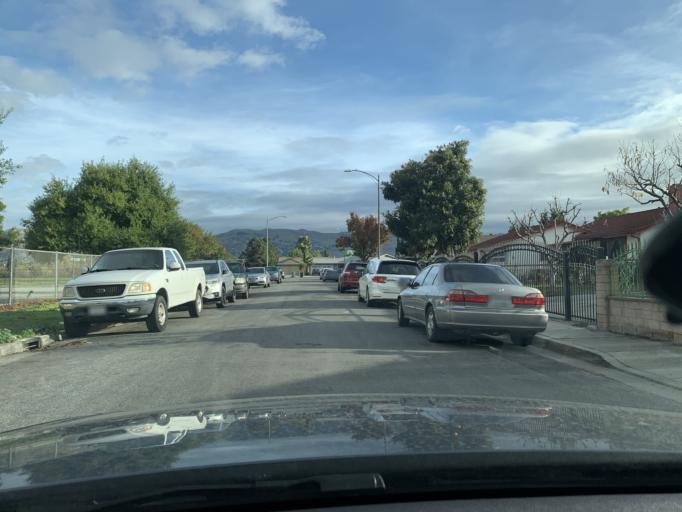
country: US
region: California
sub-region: Santa Clara County
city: Alum Rock
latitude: 37.3492
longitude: -121.8407
